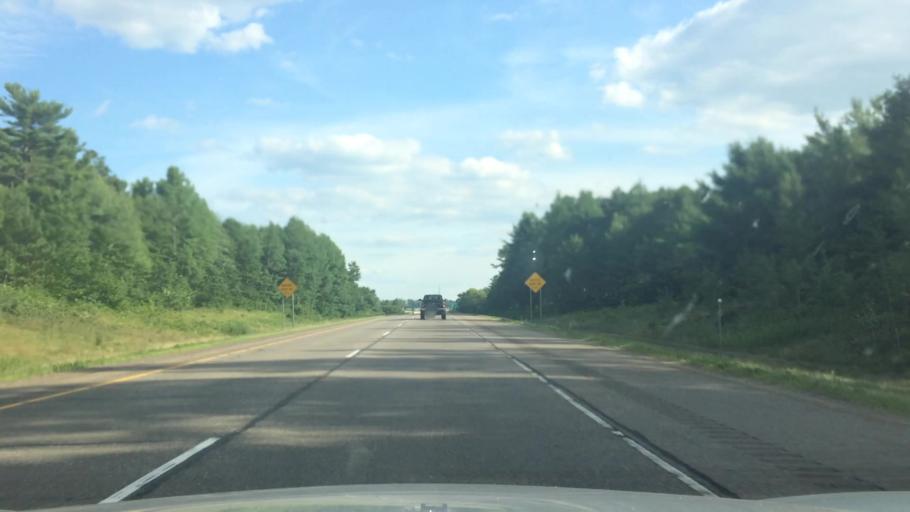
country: US
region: Wisconsin
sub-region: Lincoln County
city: Merrill
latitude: 45.1424
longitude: -89.6416
